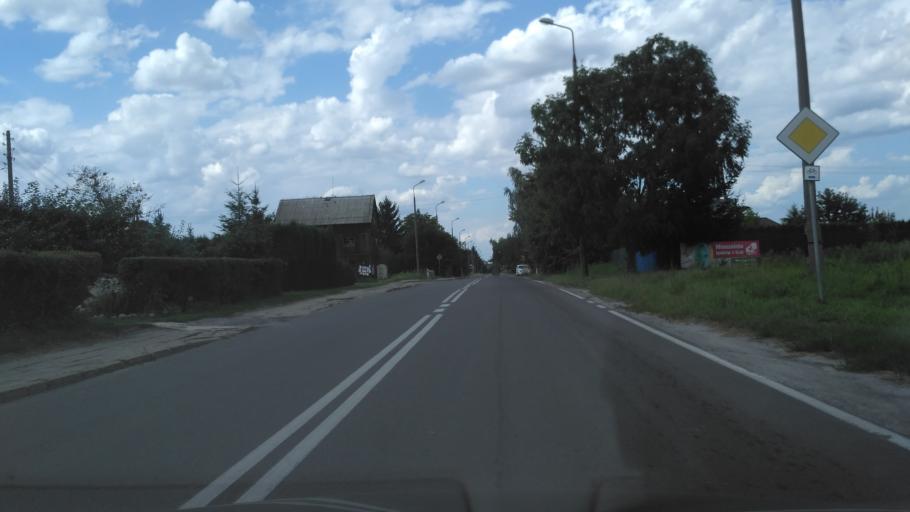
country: PL
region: Lublin Voivodeship
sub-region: Powiat leczynski
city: Milejow
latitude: 51.2125
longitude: 22.9318
